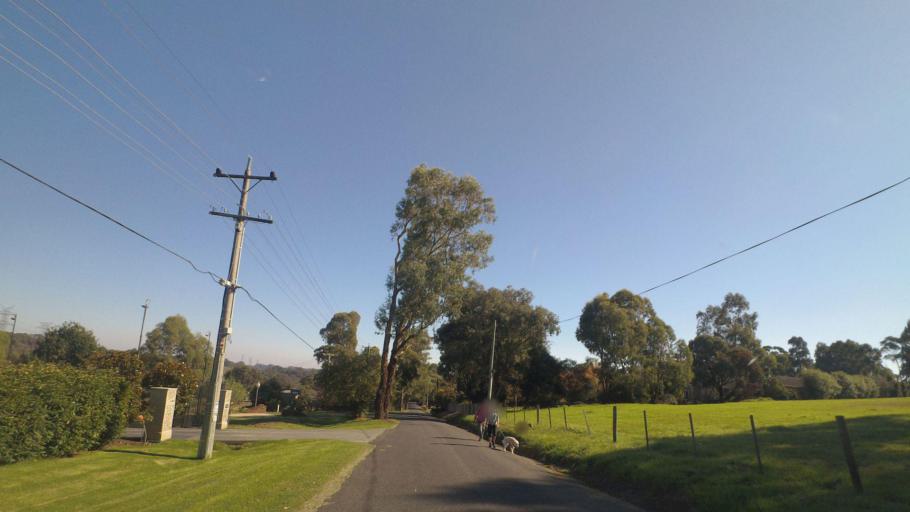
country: AU
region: Victoria
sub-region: Nillumbik
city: Eltham
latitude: -37.7435
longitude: 145.1585
